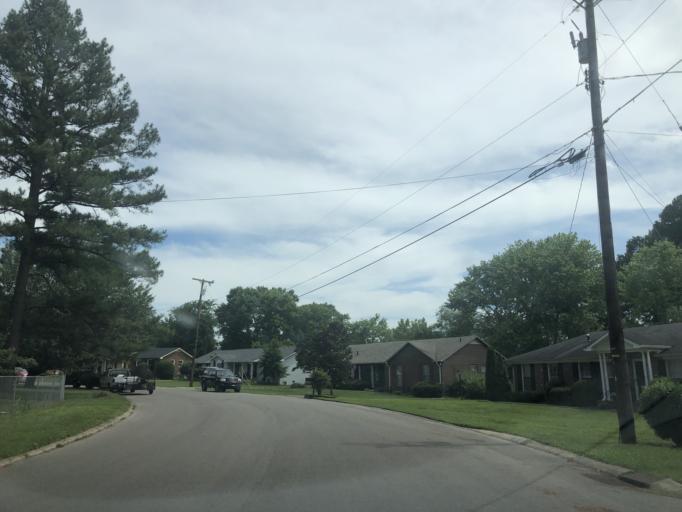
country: US
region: Tennessee
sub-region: Davidson County
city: Belle Meade
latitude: 36.0790
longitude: -86.9394
